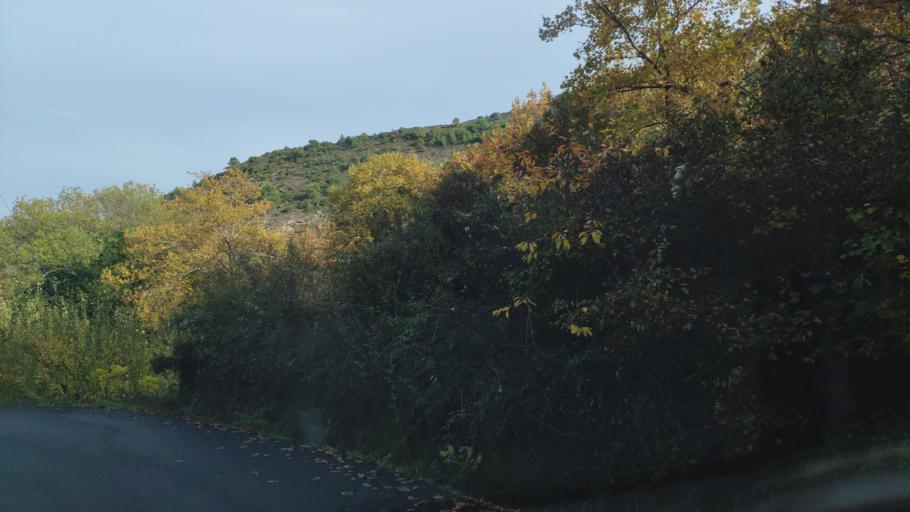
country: GR
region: West Greece
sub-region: Nomos Achaias
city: Aiyira
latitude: 38.0678
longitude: 22.3922
